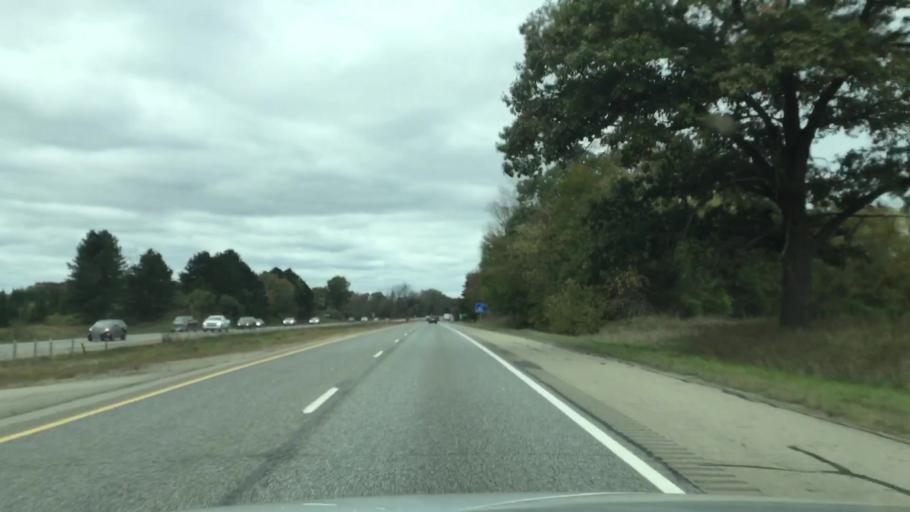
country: US
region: Michigan
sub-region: Jackson County
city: Grass Lake
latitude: 42.2972
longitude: -84.1271
